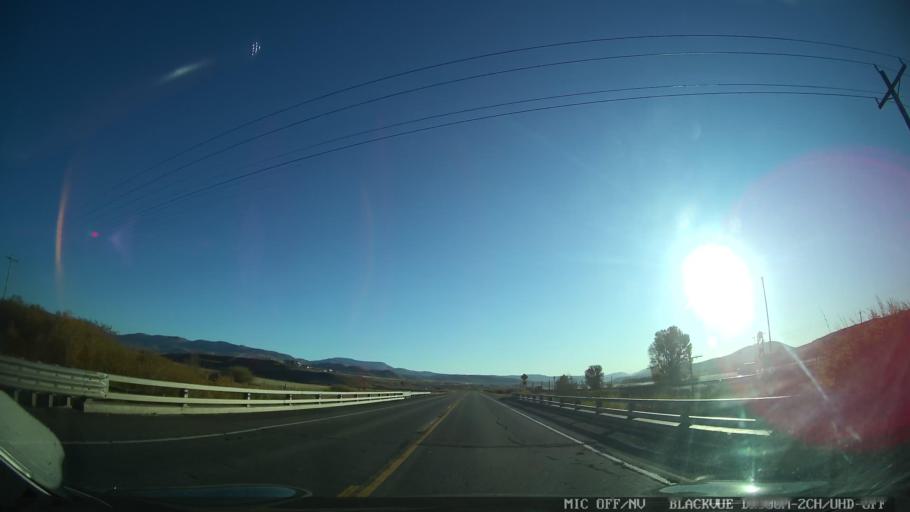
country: US
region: Colorado
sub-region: Grand County
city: Kremmling
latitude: 40.0588
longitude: -106.3063
